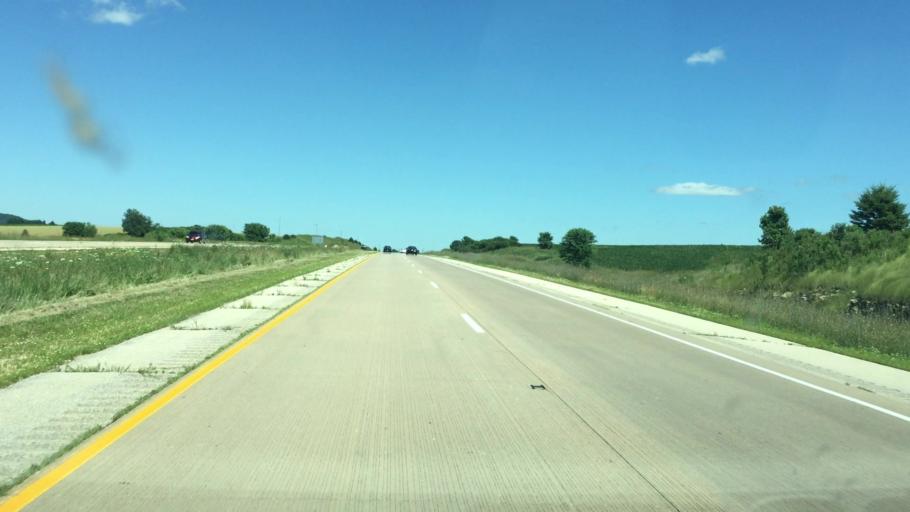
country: US
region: Wisconsin
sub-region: Grant County
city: Platteville
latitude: 42.7386
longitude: -90.4041
